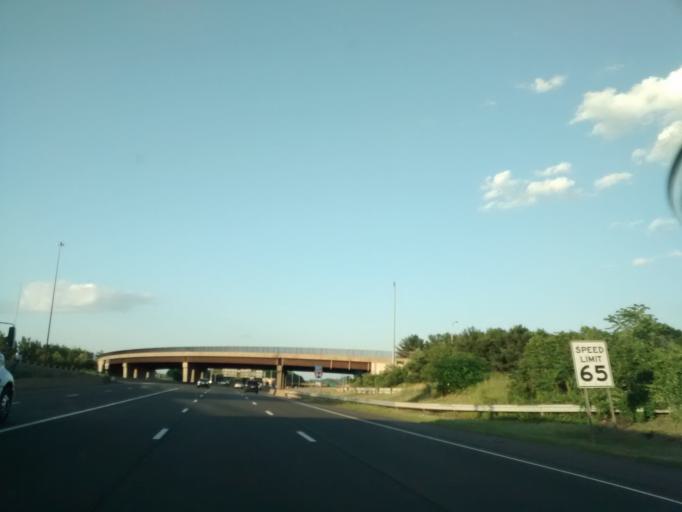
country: US
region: Connecticut
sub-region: Hartford County
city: East Hartford
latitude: 41.7644
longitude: -72.6286
